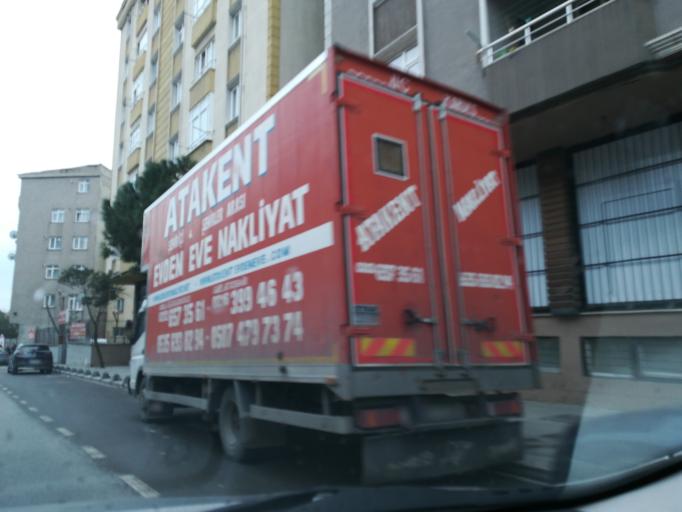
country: TR
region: Istanbul
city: Bagcilar
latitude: 41.0376
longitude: 28.8416
